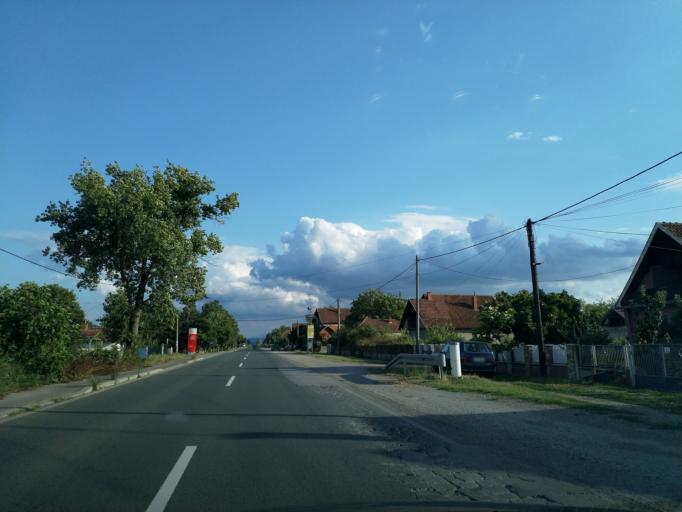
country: RS
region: Central Serbia
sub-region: Pomoravski Okrug
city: Paracin
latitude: 43.8055
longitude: 21.4212
